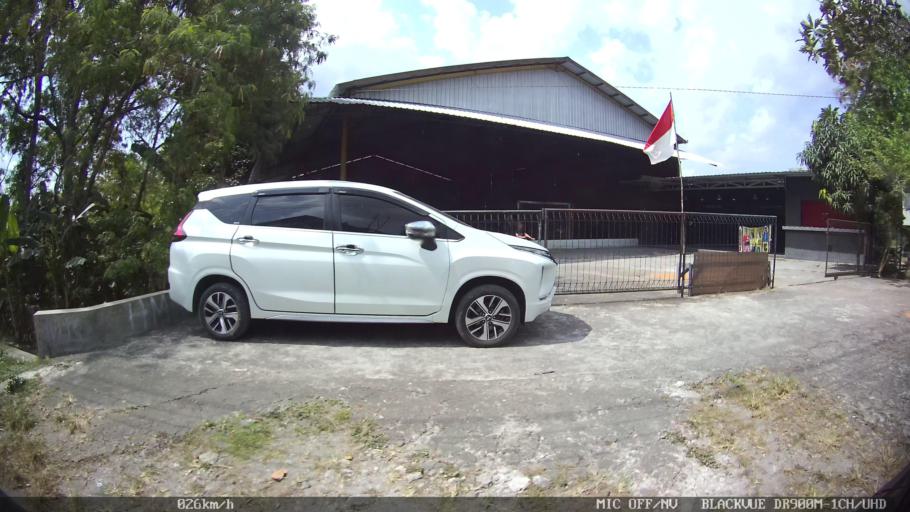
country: ID
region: Daerah Istimewa Yogyakarta
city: Kasihan
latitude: -7.8109
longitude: 110.3356
